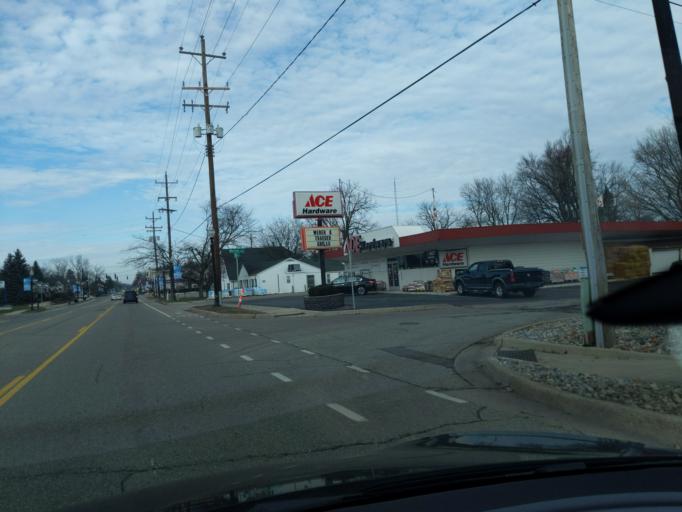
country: US
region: Michigan
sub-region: Ingham County
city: Holt
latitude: 42.6390
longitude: -84.5138
